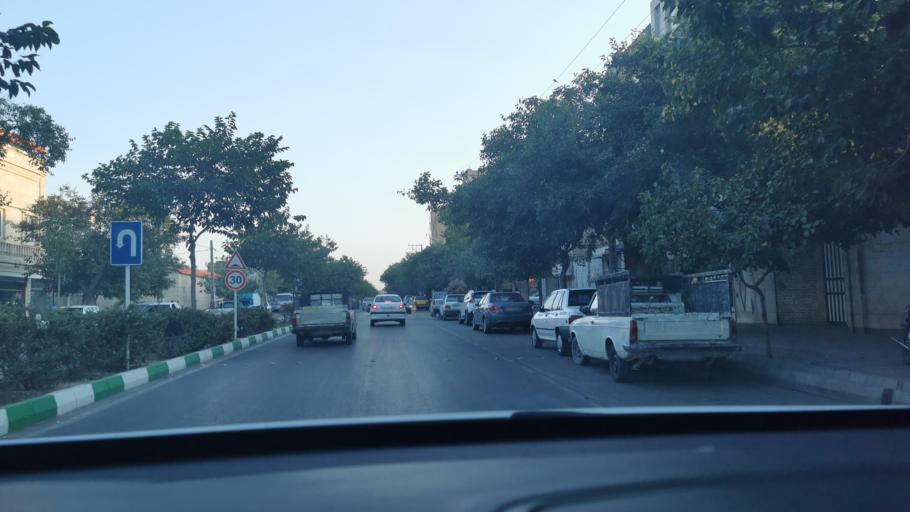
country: IR
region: Razavi Khorasan
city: Mashhad
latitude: 36.3186
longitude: 59.6383
